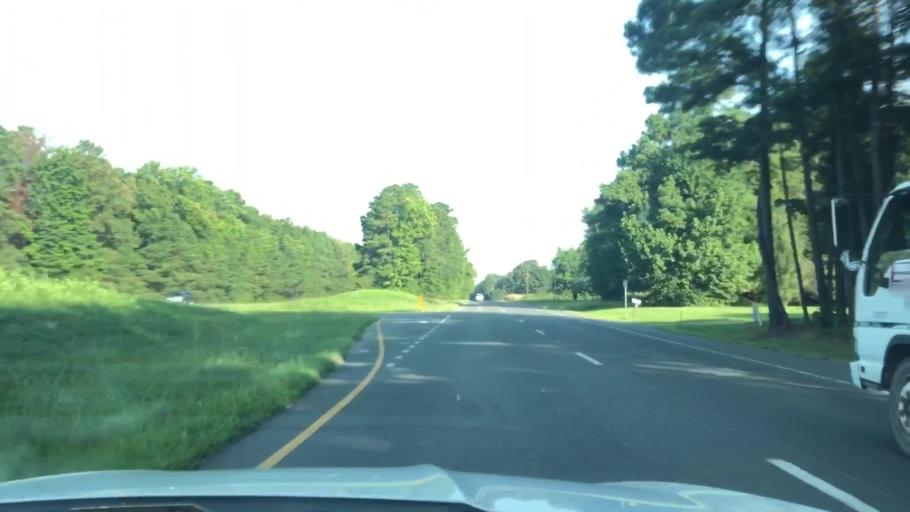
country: US
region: Virginia
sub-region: King and Queen County
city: King and Queen Court House
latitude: 37.7604
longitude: -76.7269
